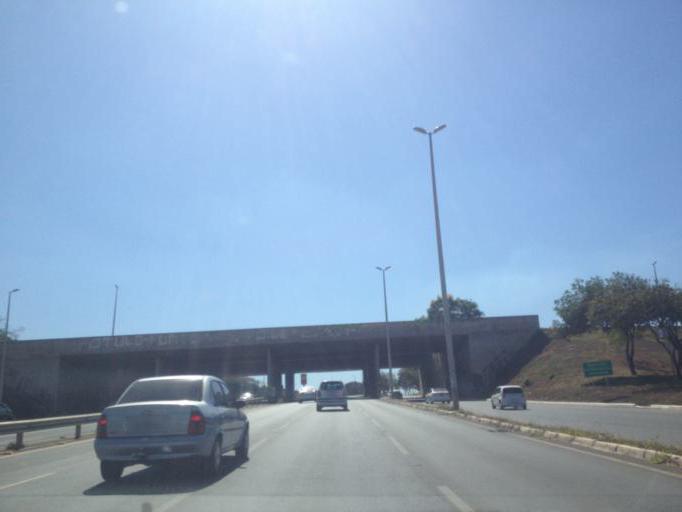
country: BR
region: Federal District
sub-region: Brasilia
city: Brasilia
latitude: -15.8462
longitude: -47.9314
